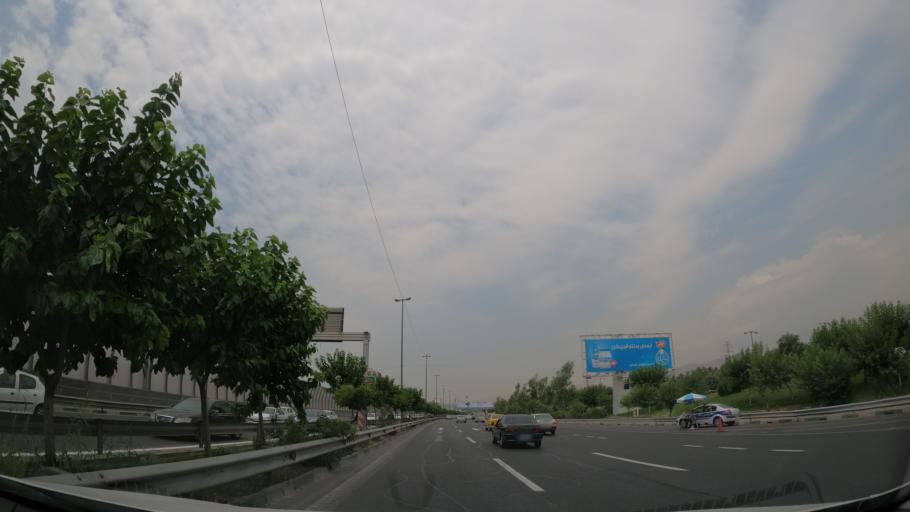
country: IR
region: Tehran
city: Tehran
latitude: 35.7389
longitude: 51.3607
